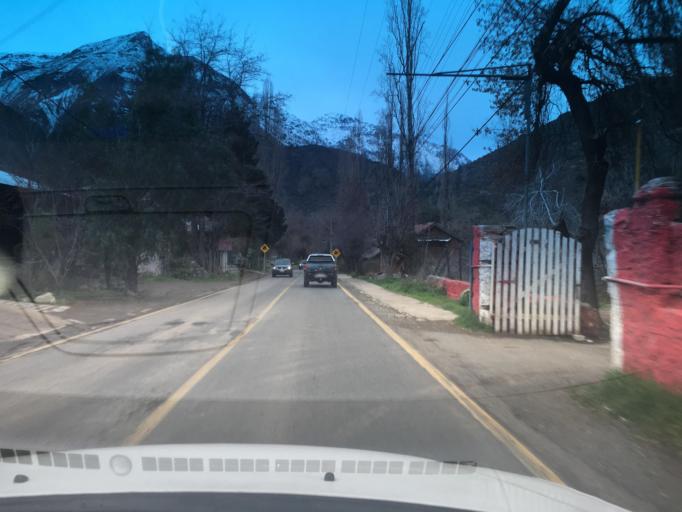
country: CL
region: Santiago Metropolitan
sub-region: Provincia de Cordillera
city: Puente Alto
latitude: -33.7327
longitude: -70.3113
